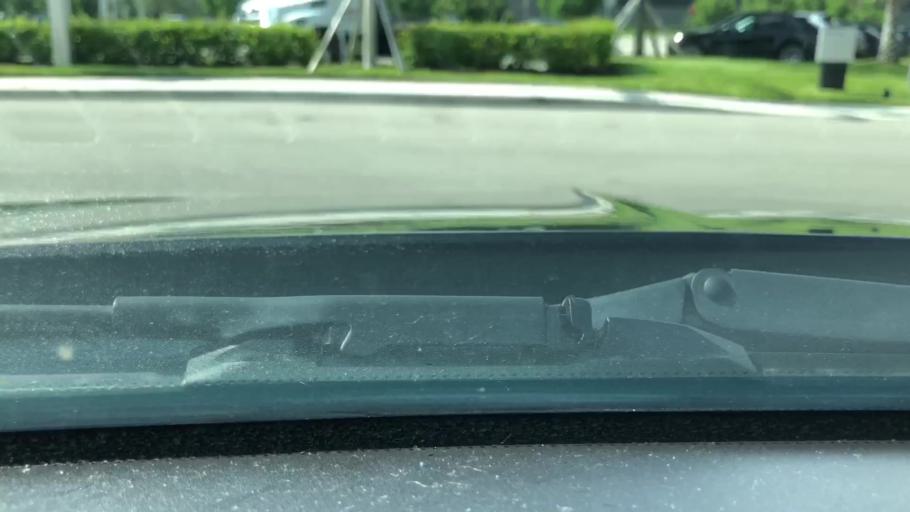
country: US
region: Florida
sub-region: Broward County
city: Kendall Green
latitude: 26.2598
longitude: -80.1280
